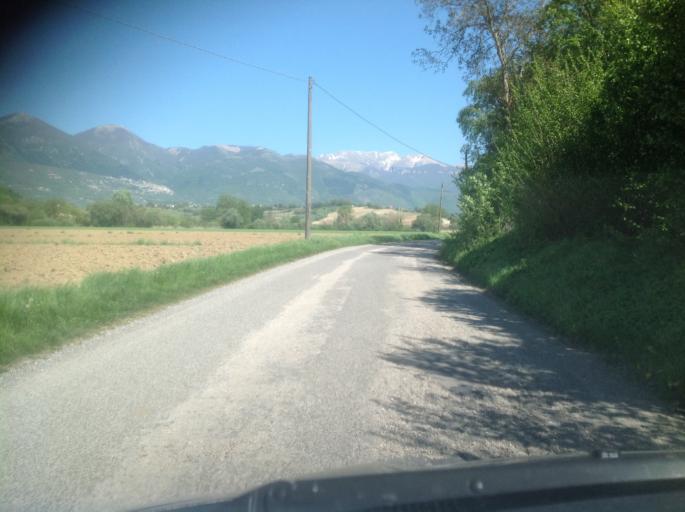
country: IT
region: Latium
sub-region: Provincia di Rieti
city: Colli sul Velino
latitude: 42.4861
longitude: 12.8062
